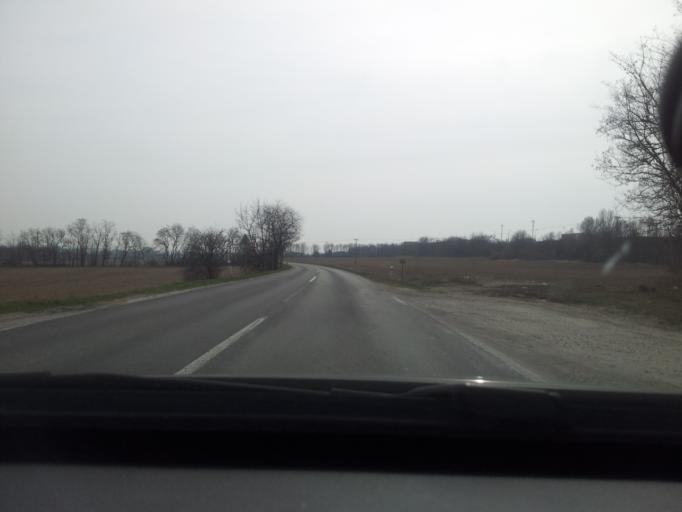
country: SK
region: Trnavsky
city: Hlohovec
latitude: 48.3823
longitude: 17.8710
